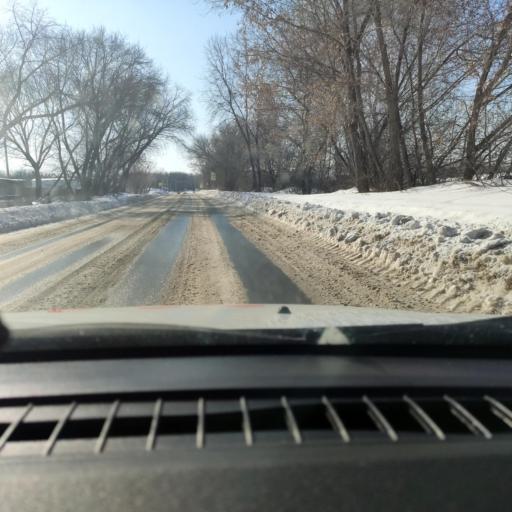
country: RU
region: Samara
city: Novokuybyshevsk
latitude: 53.1211
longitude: 49.9175
